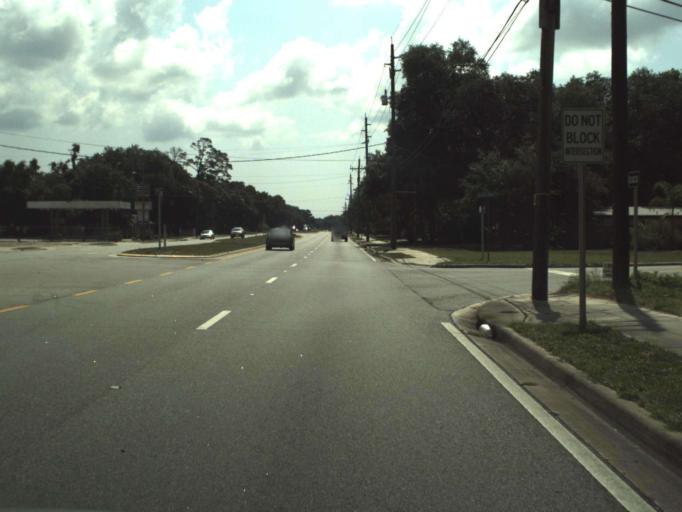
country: US
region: Florida
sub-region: Volusia County
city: Glencoe
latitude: 29.0133
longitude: -80.9561
